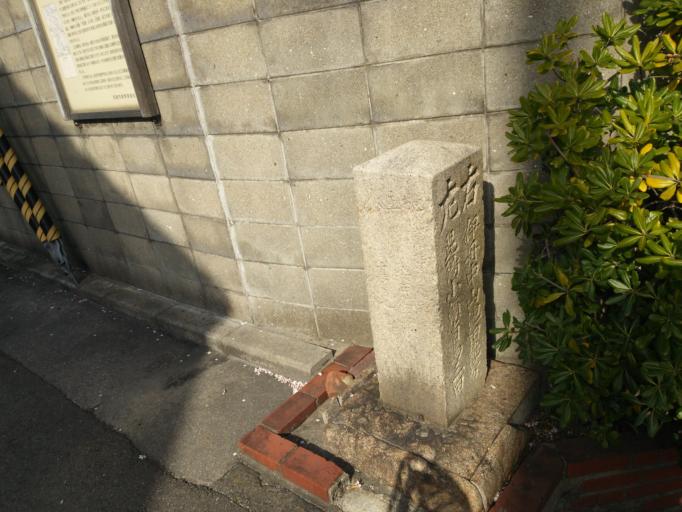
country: JP
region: Hyogo
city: Amagasaki
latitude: 34.7379
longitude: 135.4447
